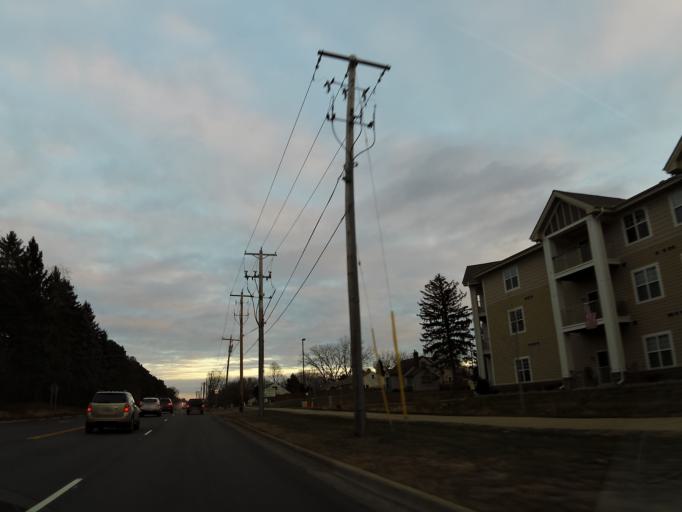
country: US
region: Minnesota
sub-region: Ramsey County
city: Vadnais Heights
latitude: 45.0503
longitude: -93.0479
